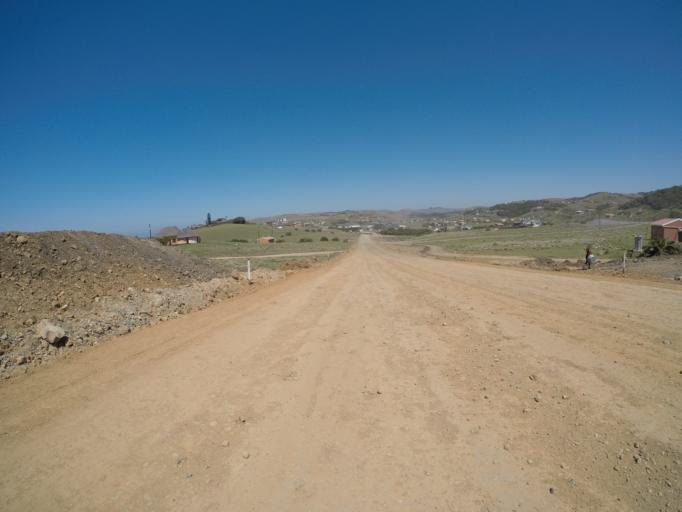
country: ZA
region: Eastern Cape
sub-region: OR Tambo District Municipality
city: Libode
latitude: -32.0277
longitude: 29.1155
